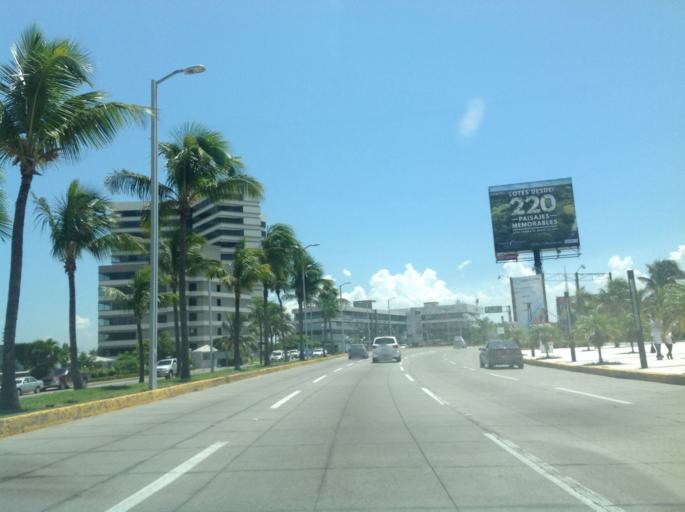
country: MX
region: Veracruz
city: Boca del Rio
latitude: 19.1377
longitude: -96.1039
